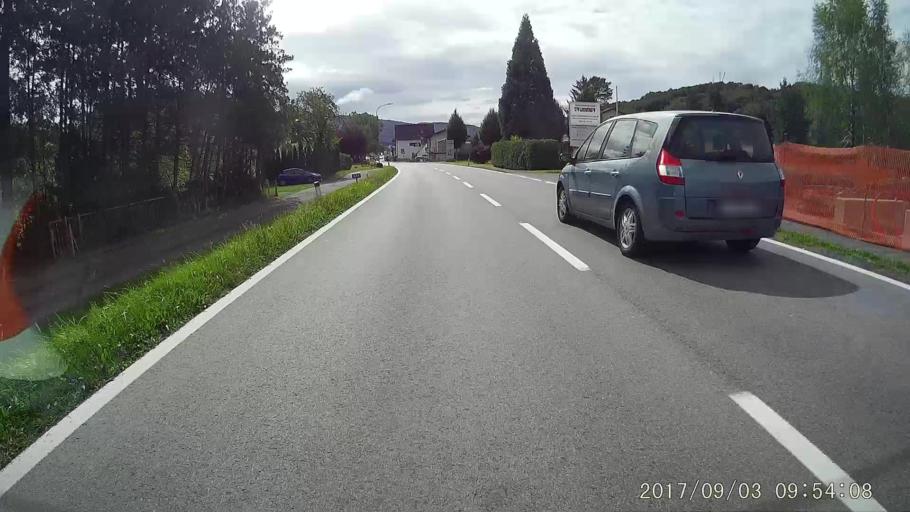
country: AT
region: Styria
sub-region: Politischer Bezirk Suedoststeiermark
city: Bad Gleichenberg
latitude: 46.8773
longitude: 15.8973
